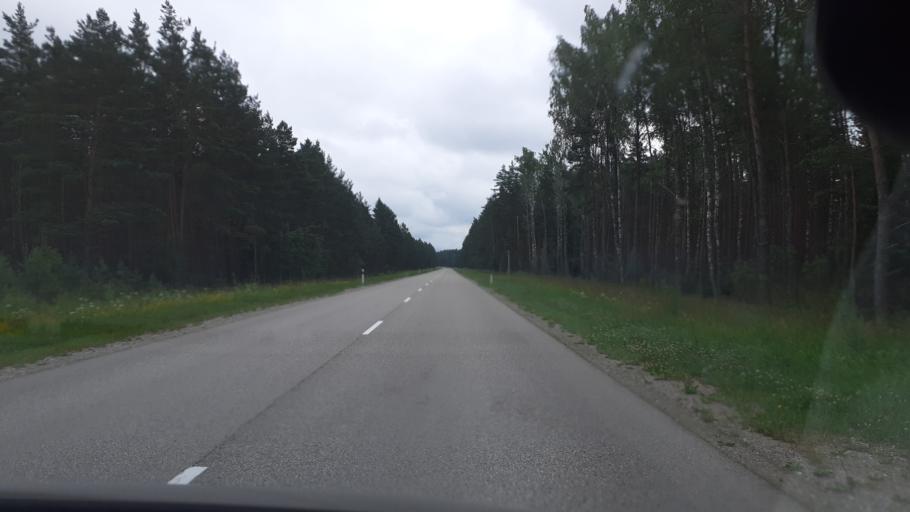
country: LV
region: Ventspils Rajons
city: Piltene
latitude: 57.1251
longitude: 21.7385
